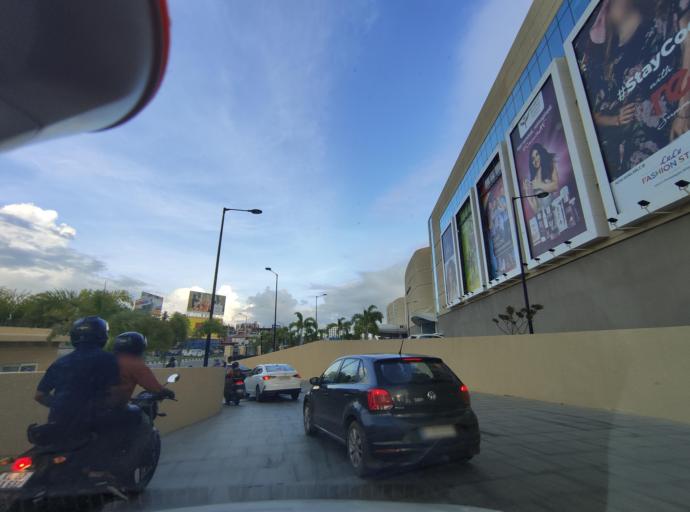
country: IN
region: Kerala
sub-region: Thiruvananthapuram
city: Thiruvananthapuram
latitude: 8.5168
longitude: 76.8984
